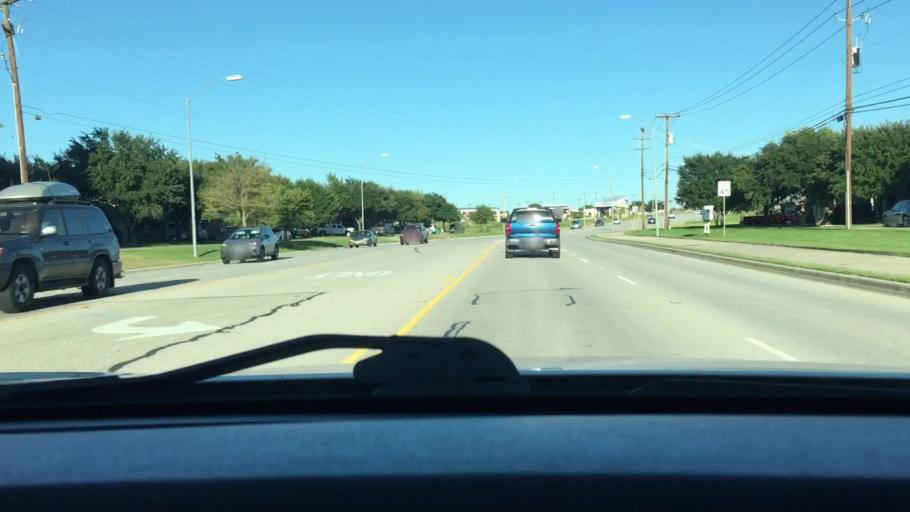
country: US
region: Texas
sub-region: Travis County
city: Windemere
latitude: 30.4722
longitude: -97.6456
